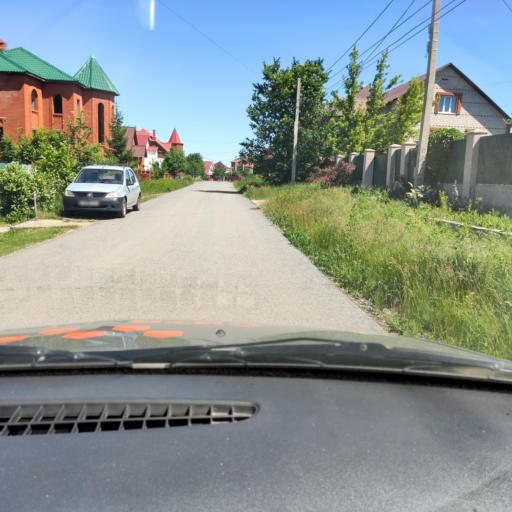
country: RU
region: Bashkortostan
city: Ufa
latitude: 54.6016
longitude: 55.9443
